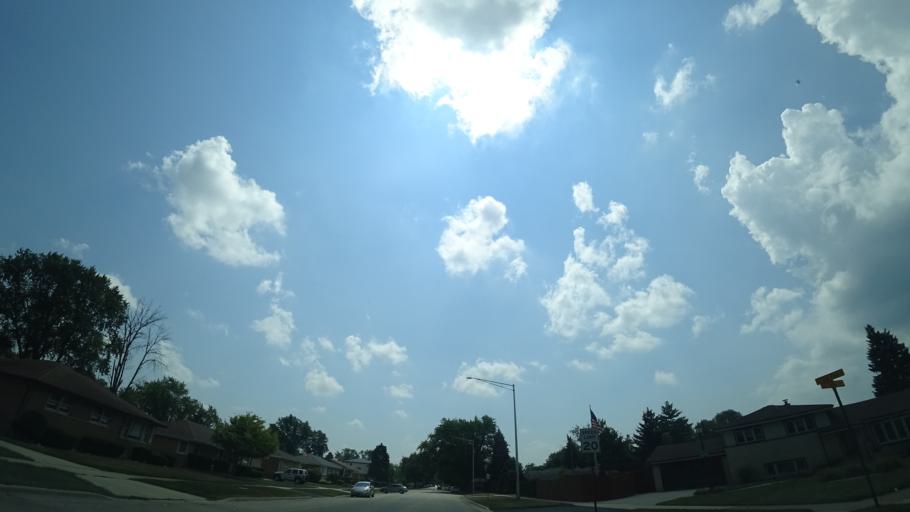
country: US
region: Illinois
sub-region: Cook County
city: Worth
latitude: 41.6957
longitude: -87.7888
